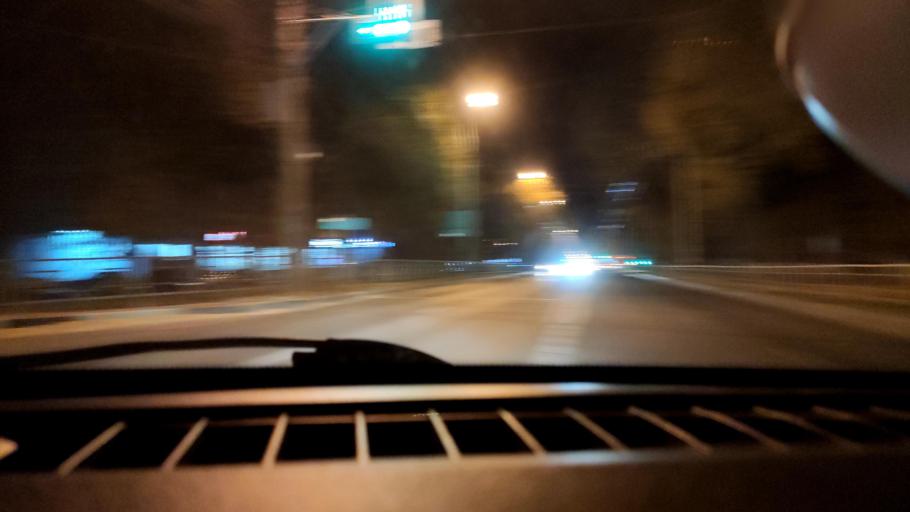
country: RU
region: Samara
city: Samara
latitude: 53.2361
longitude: 50.2418
